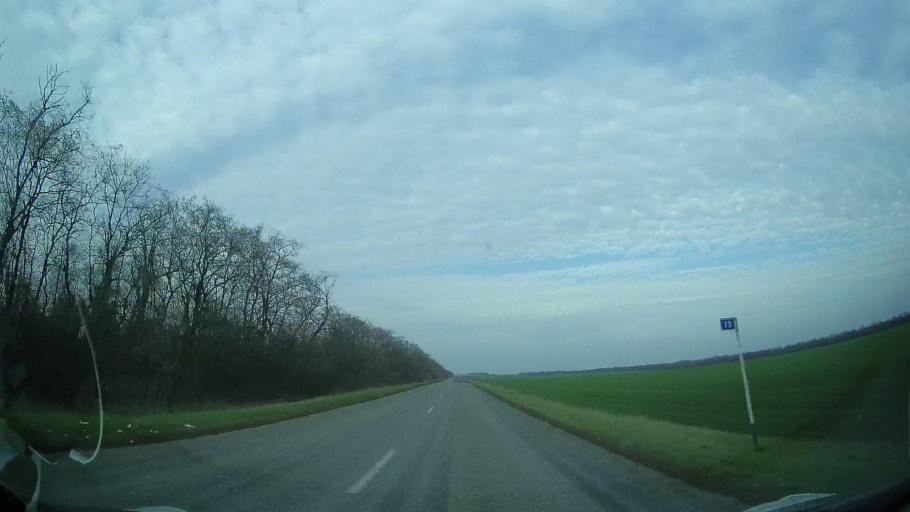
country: RU
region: Rostov
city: Zernograd
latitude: 46.9509
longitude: 40.3667
